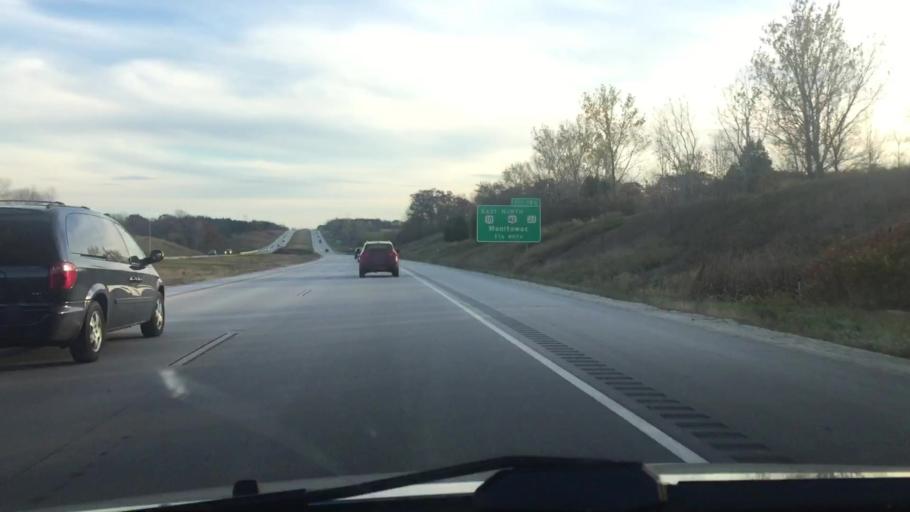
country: US
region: Wisconsin
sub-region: Manitowoc County
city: Manitowoc
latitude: 44.1332
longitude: -87.7331
